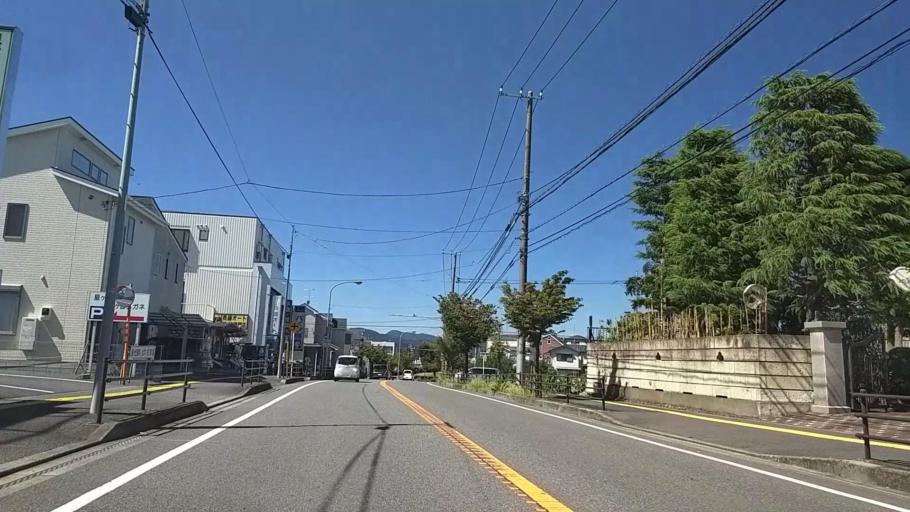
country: JP
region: Kanagawa
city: Zama
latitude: 35.5576
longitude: 139.3679
